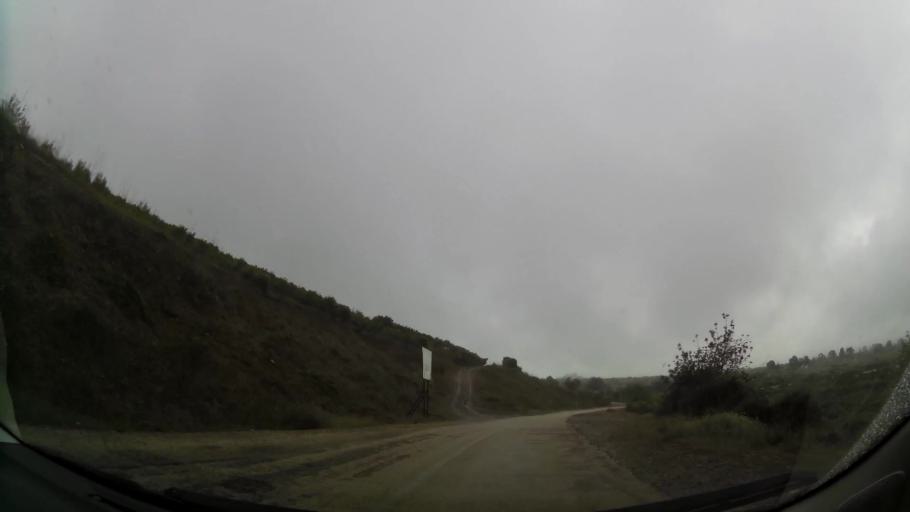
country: MA
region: Taza-Al Hoceima-Taounate
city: Imzourene
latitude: 35.1181
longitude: -3.7768
